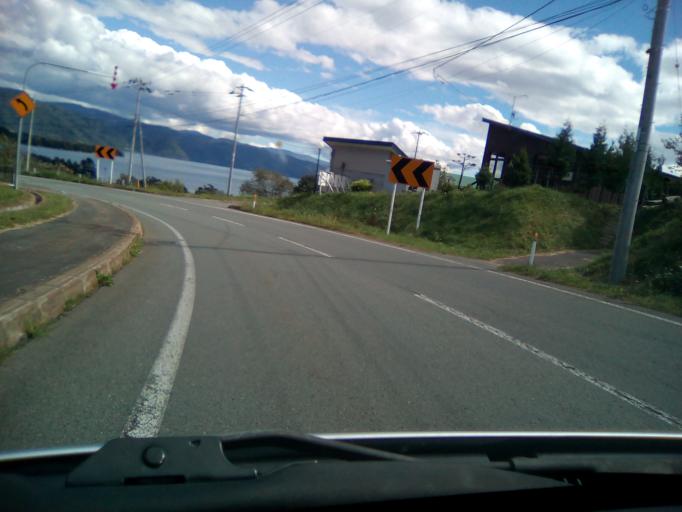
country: JP
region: Hokkaido
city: Date
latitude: 42.6455
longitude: 140.8236
